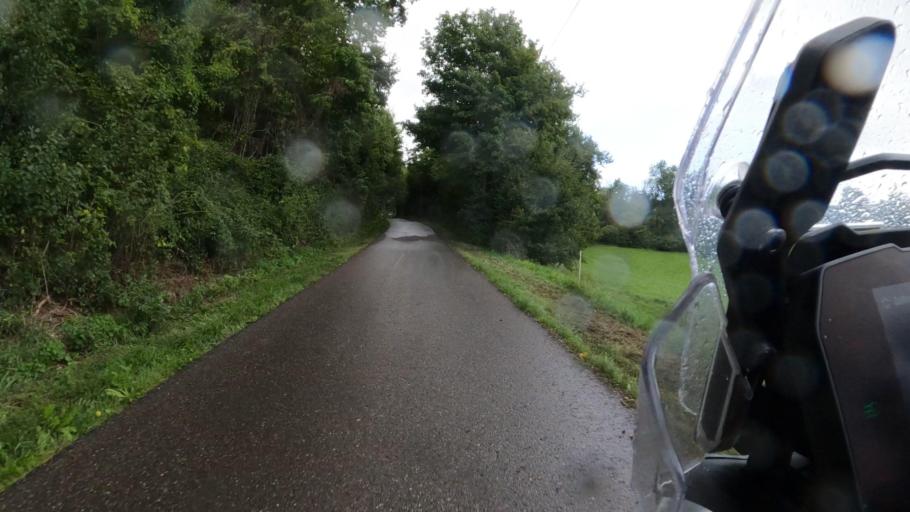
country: DE
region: Baden-Wuerttemberg
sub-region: Freiburg Region
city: Eggingen
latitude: 47.6701
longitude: 8.4026
